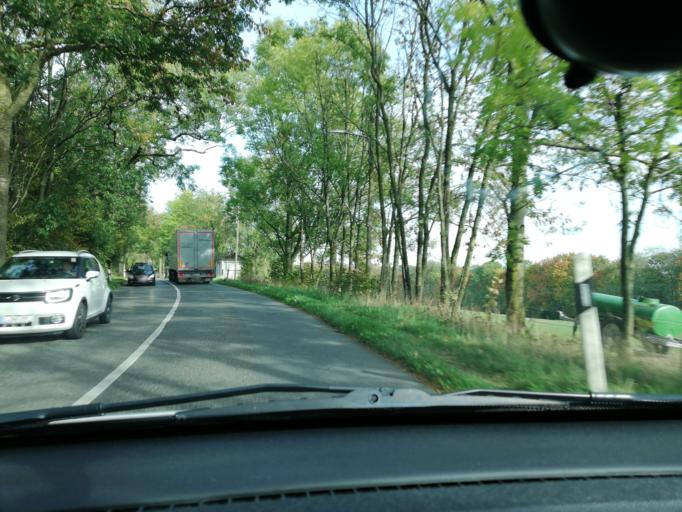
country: DE
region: North Rhine-Westphalia
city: Sprockhovel
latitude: 51.3059
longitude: 7.2300
